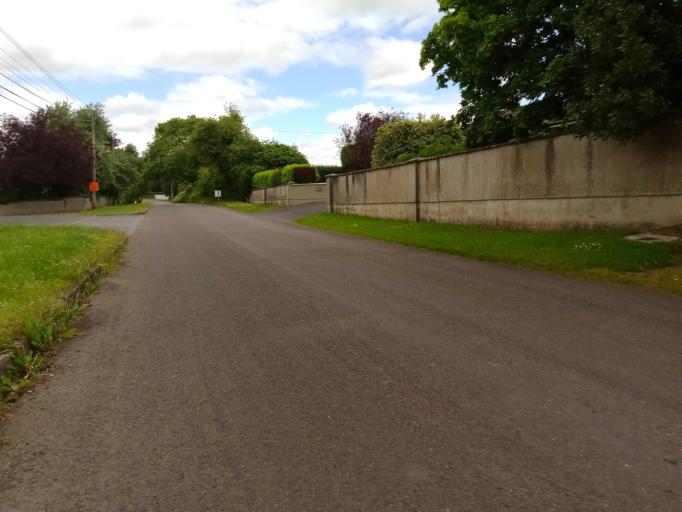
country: IE
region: Leinster
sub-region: Kilkenny
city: Kilkenny
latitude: 52.6822
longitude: -7.2489
